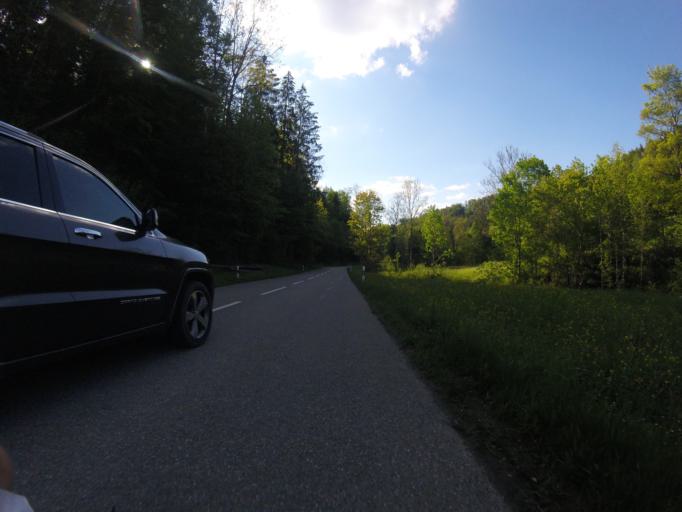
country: CH
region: Saint Gallen
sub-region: Wahlkreis Toggenburg
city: Mogelsberg
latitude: 47.3618
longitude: 9.1518
